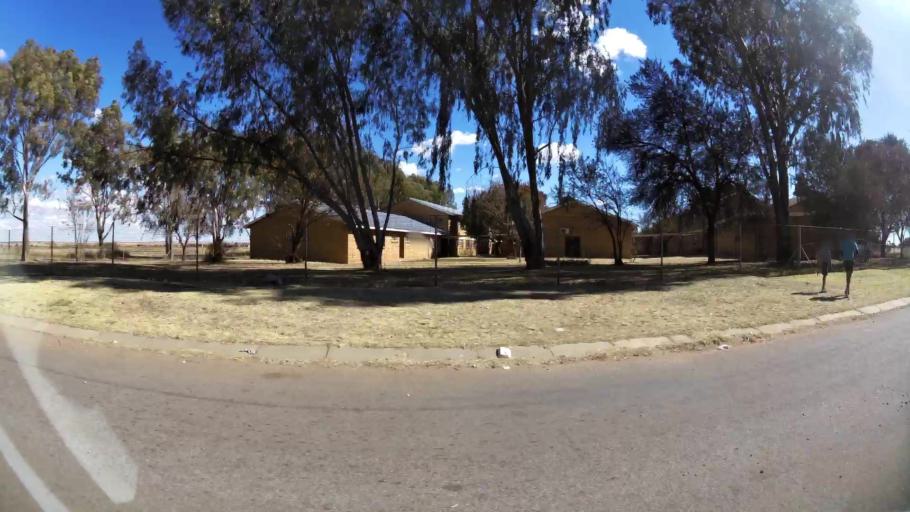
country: ZA
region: North-West
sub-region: Dr Kenneth Kaunda District Municipality
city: Klerksdorp
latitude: -26.8716
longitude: 26.5799
